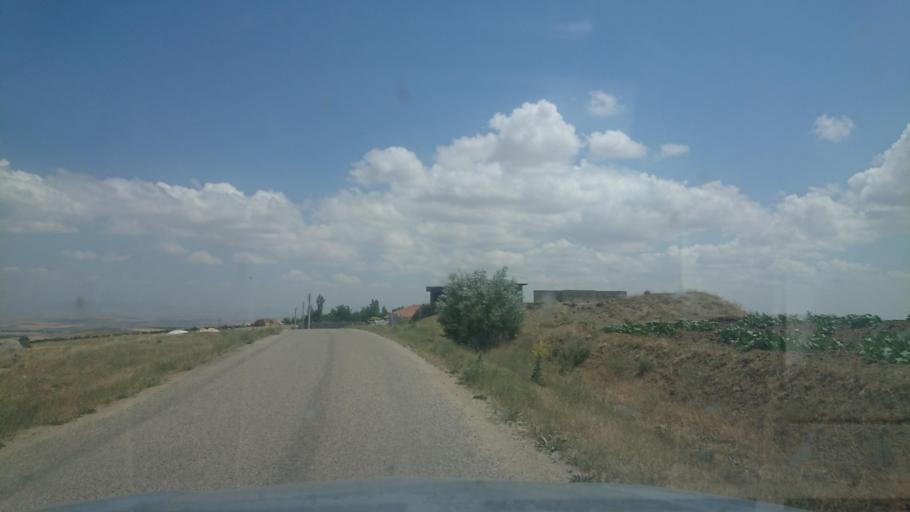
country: TR
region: Aksaray
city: Agacoren
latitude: 38.8721
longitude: 33.9413
